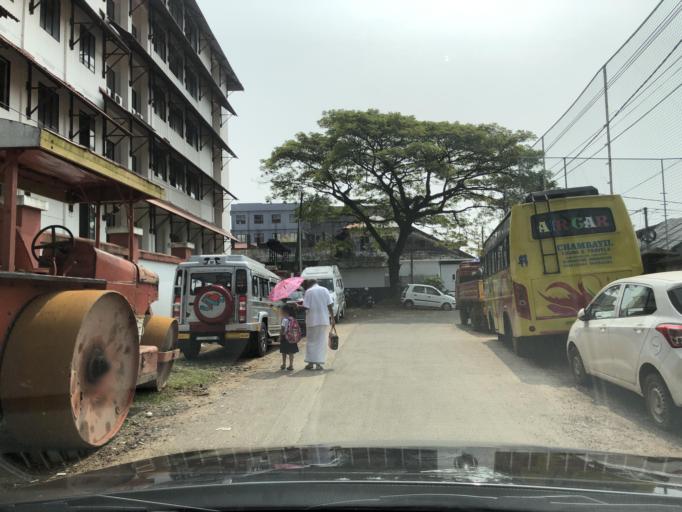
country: IN
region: Kerala
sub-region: Kozhikode
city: Kozhikode
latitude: 11.2525
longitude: 75.7747
